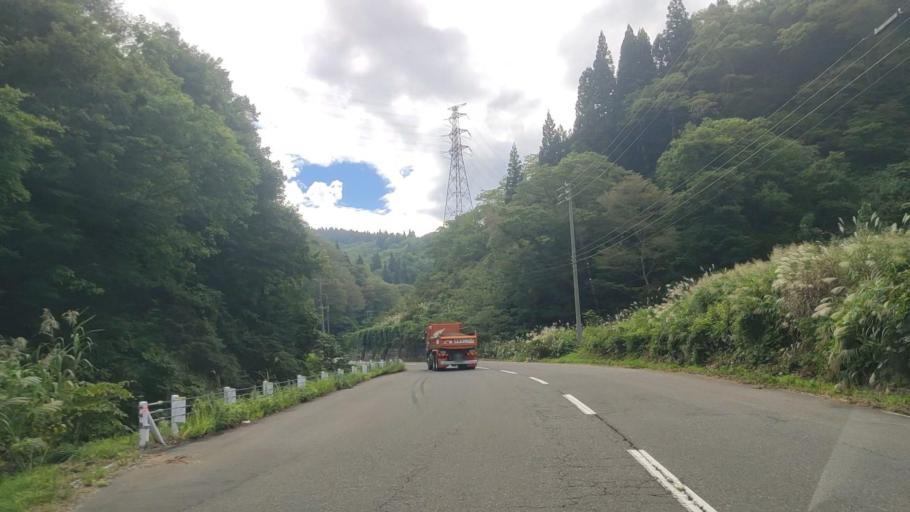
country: JP
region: Nagano
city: Iiyama
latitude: 36.8924
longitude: 138.3226
